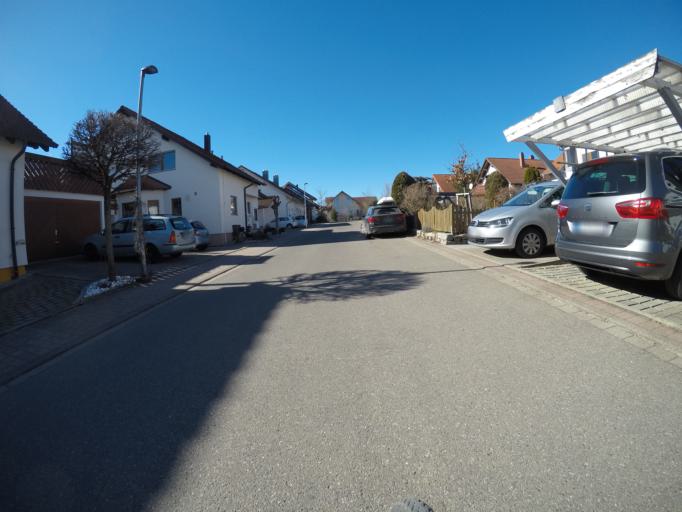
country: DE
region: Baden-Wuerttemberg
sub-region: Regierungsbezirk Stuttgart
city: Herrenberg
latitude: 48.5660
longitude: 8.8485
